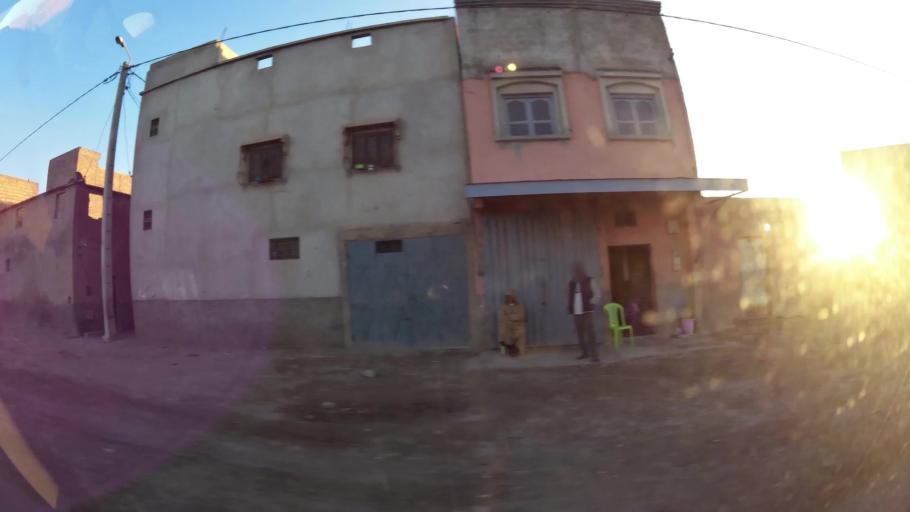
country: MA
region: Marrakech-Tensift-Al Haouz
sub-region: Kelaa-Des-Sraghna
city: Sidi Abdallah
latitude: 32.2396
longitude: -7.9358
